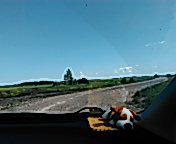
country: RU
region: Penza
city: Lermontovo
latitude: 52.9826
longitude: 43.6665
